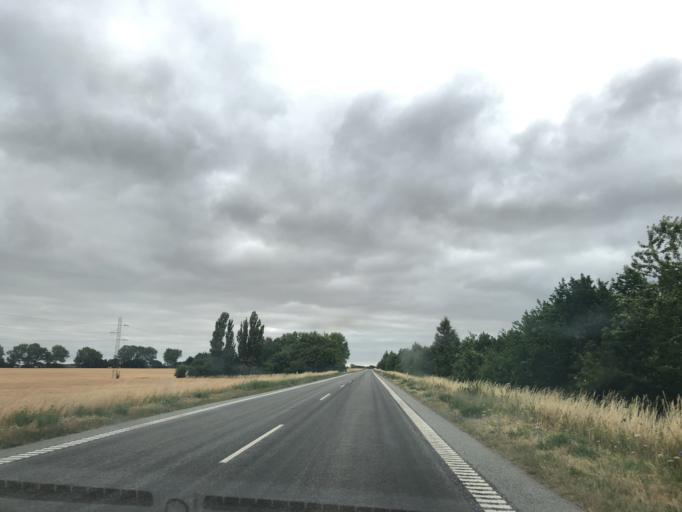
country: DK
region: Zealand
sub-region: Slagelse Kommune
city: Skaelskor
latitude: 55.2141
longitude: 11.2684
